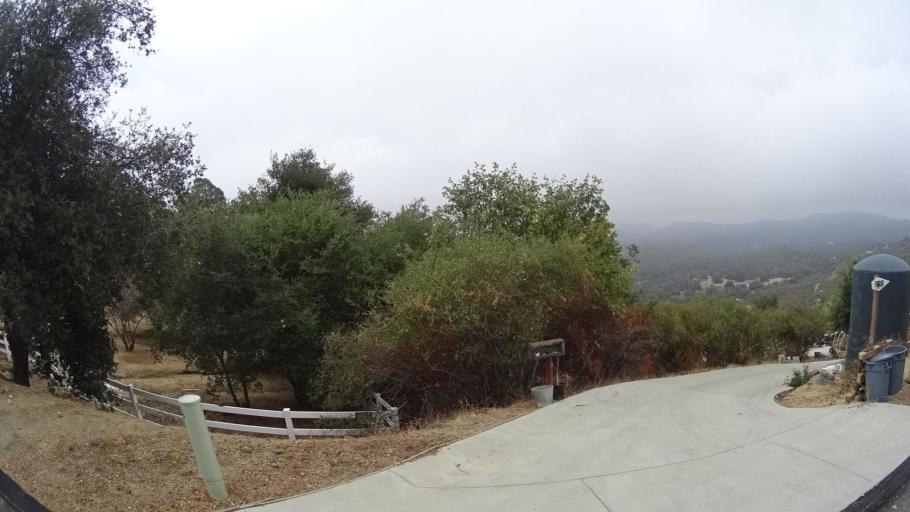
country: US
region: California
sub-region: San Diego County
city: Julian
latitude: 33.0089
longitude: -116.6139
